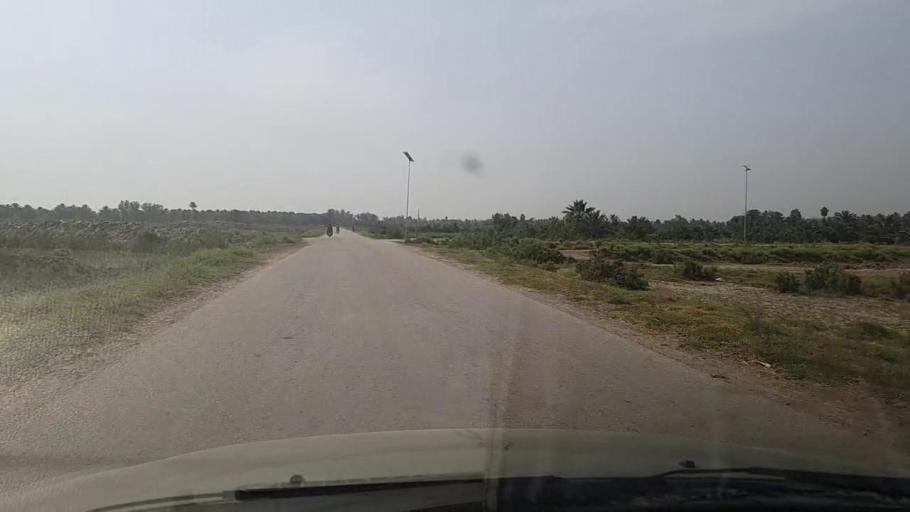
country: PK
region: Sindh
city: Gambat
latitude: 27.4595
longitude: 68.4828
